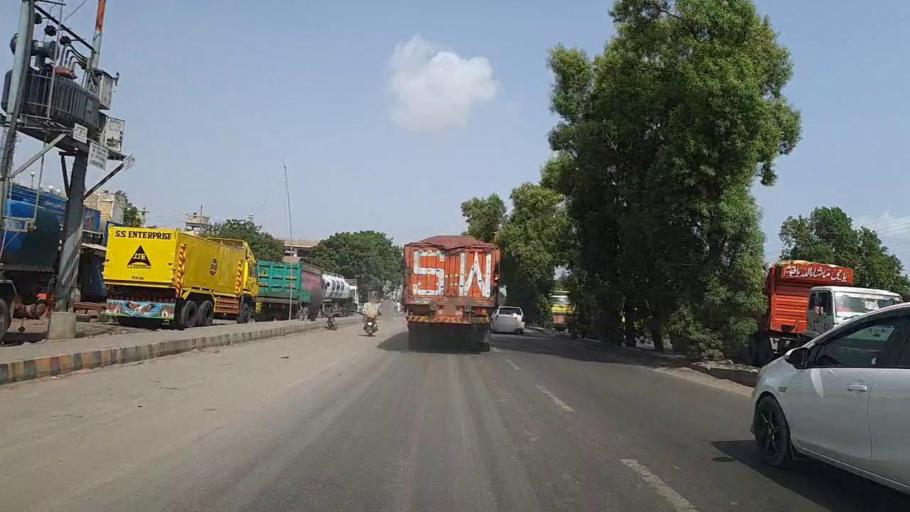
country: PK
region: Sindh
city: Malir Cantonment
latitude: 24.8652
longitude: 67.3104
